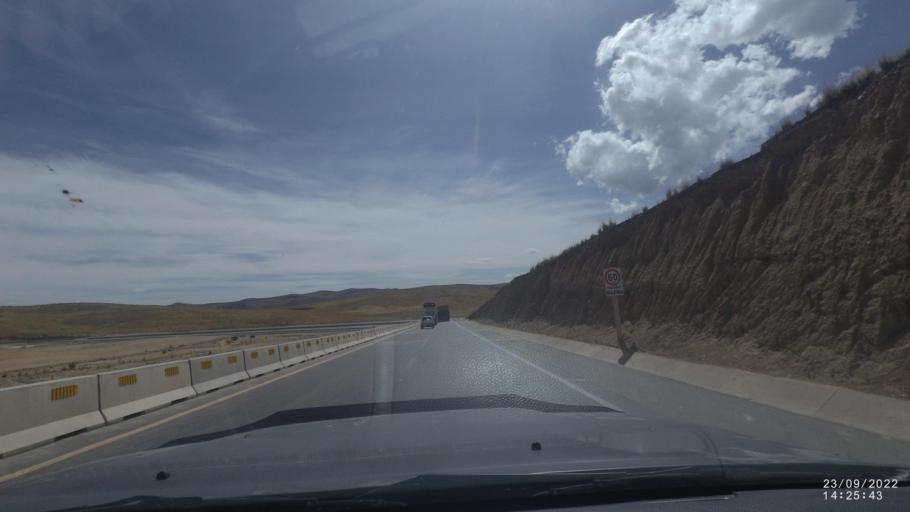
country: BO
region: Cochabamba
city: Colchani
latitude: -17.6651
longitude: -66.7567
